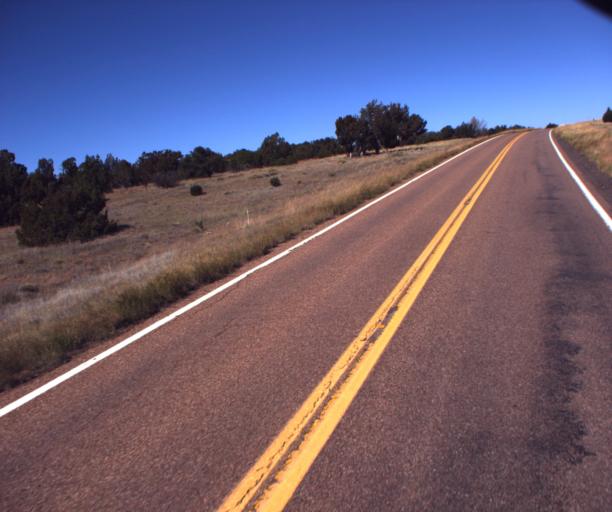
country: US
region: Arizona
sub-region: Navajo County
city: Heber-Overgaard
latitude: 34.4548
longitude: -110.4630
